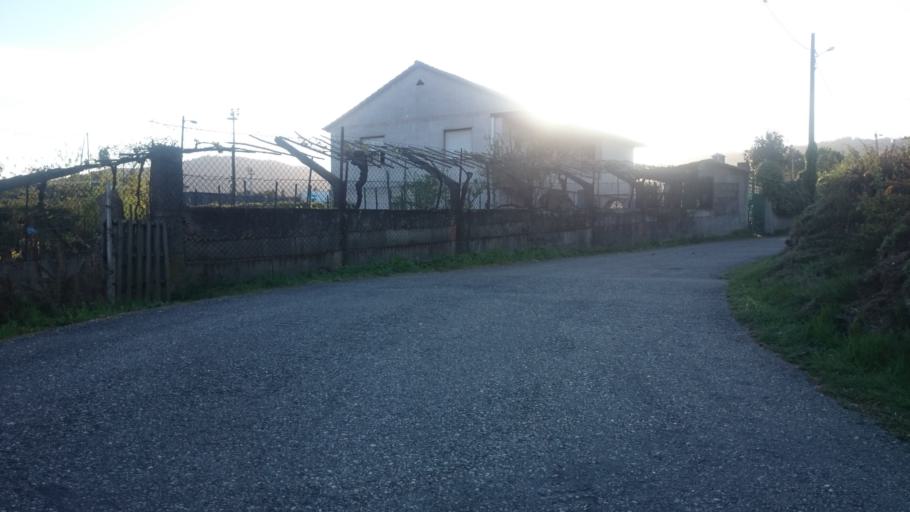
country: ES
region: Galicia
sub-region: Provincia de Pontevedra
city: Porrino
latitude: 42.1568
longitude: -8.6263
